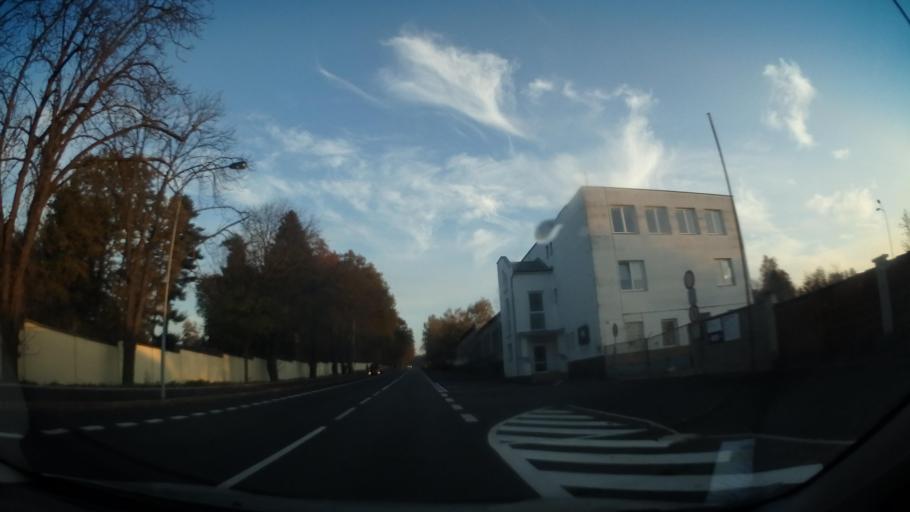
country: CZ
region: Central Bohemia
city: Vlasim
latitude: 49.6932
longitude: 14.9107
